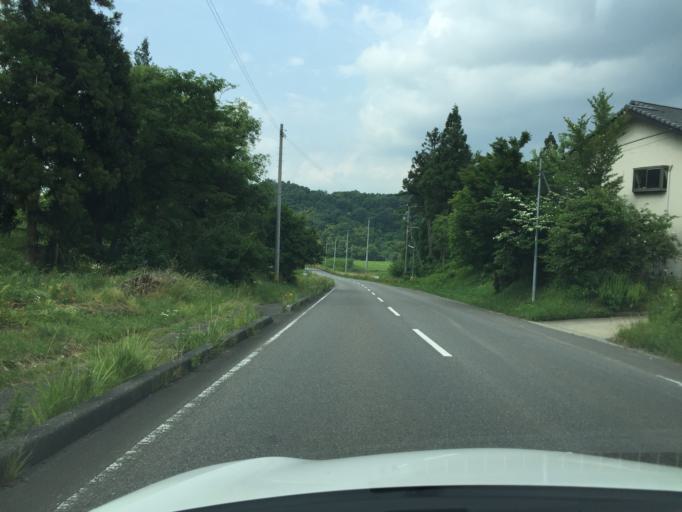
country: JP
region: Fukushima
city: Sukagawa
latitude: 37.3083
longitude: 140.4414
